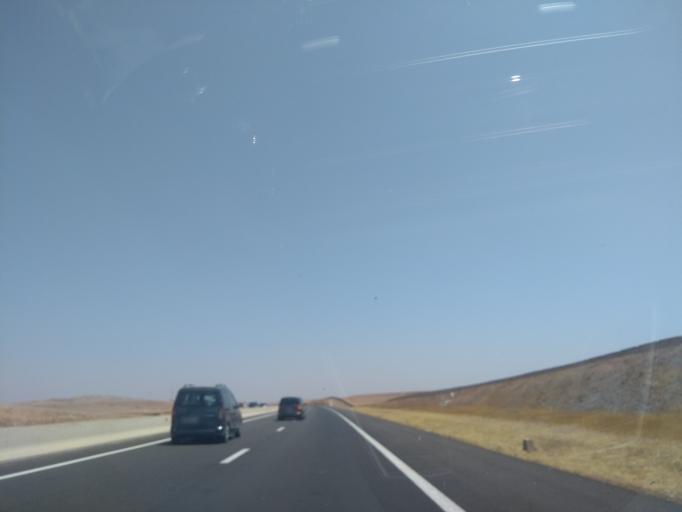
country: MA
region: Marrakech-Tensift-Al Haouz
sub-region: Kelaa-Des-Sraghna
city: Sidi Abdallah
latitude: 32.2945
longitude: -7.9612
